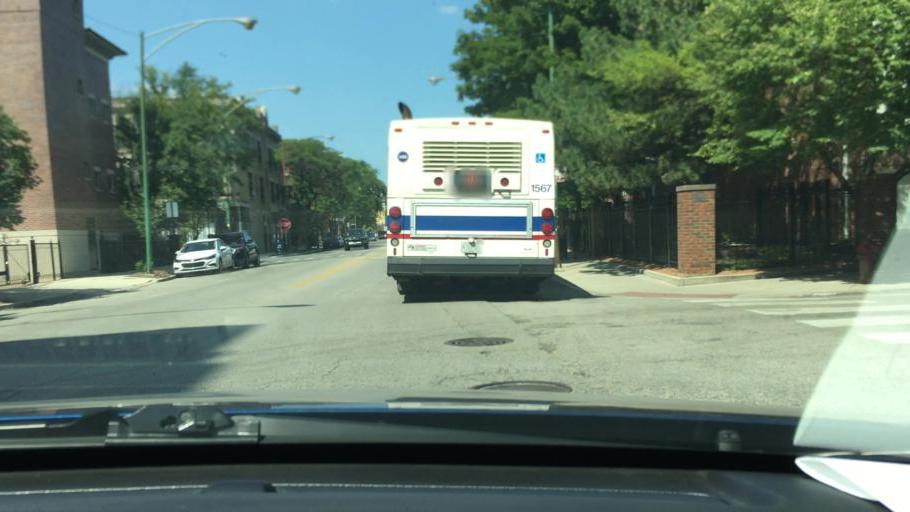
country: US
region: Illinois
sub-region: Cook County
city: Chicago
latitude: 41.8717
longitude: -87.6568
